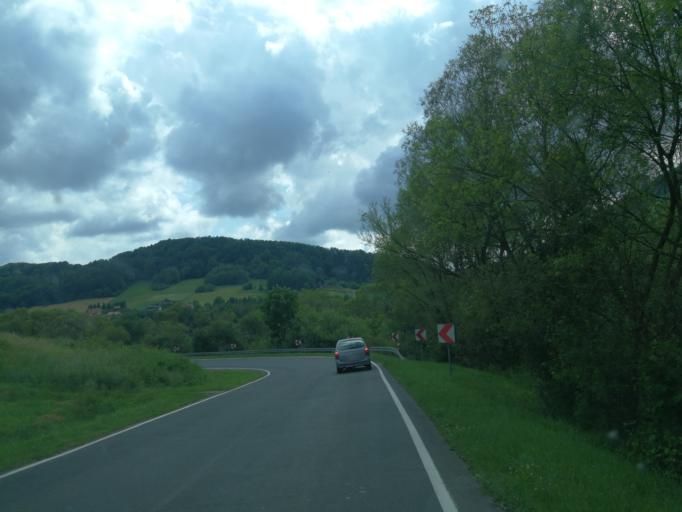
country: PL
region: Subcarpathian Voivodeship
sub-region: Powiat leski
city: Polanczyk
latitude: 49.4099
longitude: 22.4464
